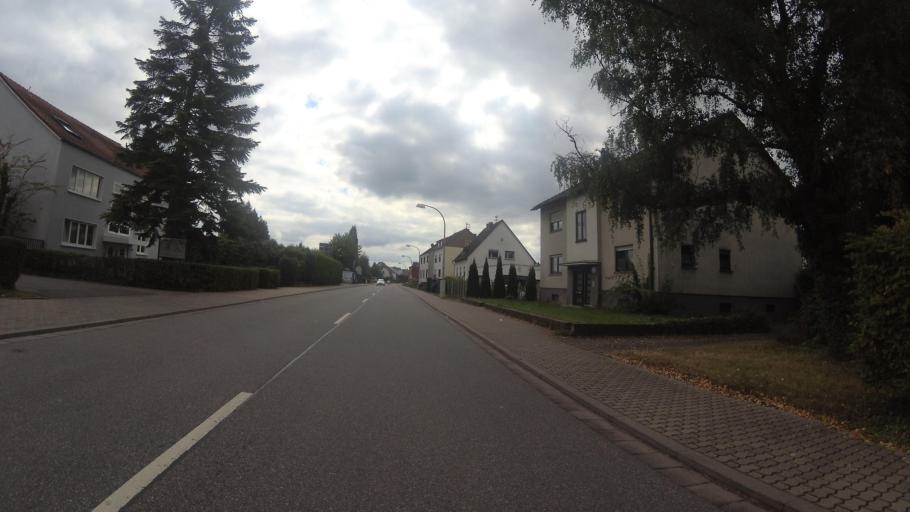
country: FR
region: Lorraine
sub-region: Departement de la Moselle
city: Schoeneck
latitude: 49.2345
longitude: 6.9028
